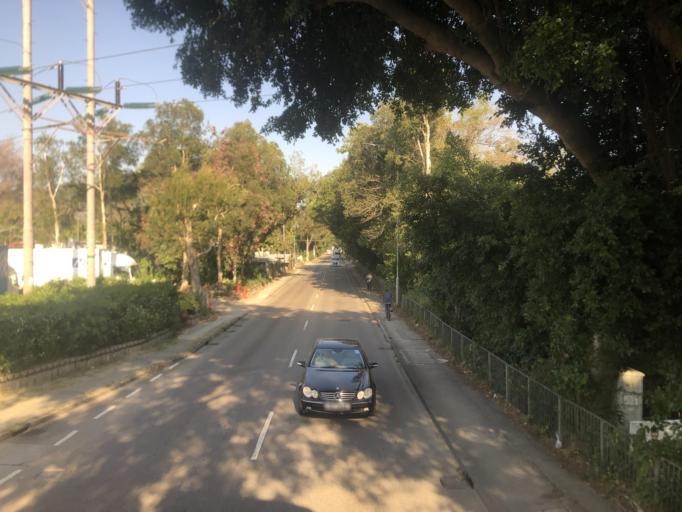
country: CN
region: Guangdong
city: Liantang
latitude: 22.5152
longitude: 114.1694
